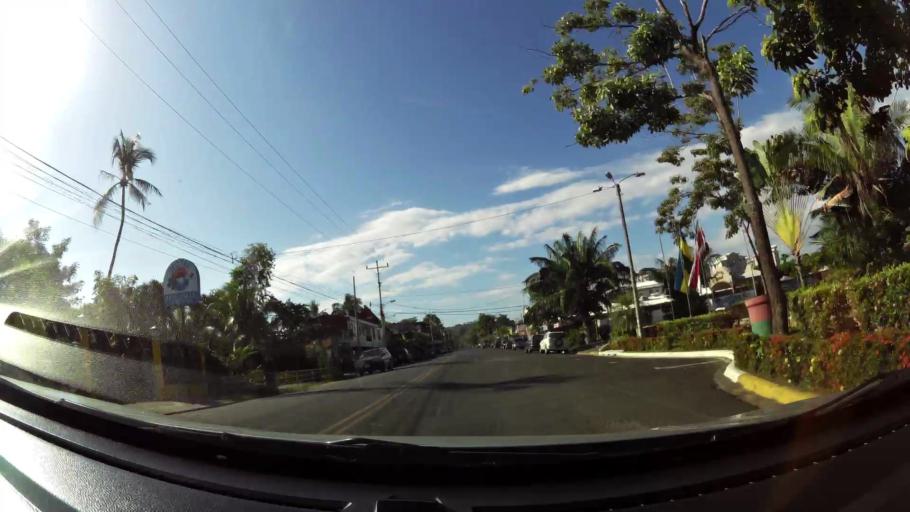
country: CR
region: Puntarenas
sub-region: Canton de Garabito
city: Jaco
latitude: 9.6178
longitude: -84.6319
